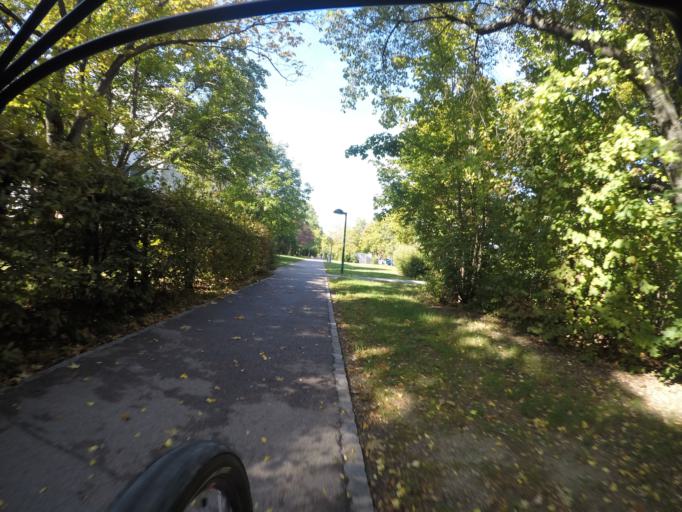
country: AT
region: Lower Austria
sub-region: Politischer Bezirk Modling
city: Wiener Neudorf
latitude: 48.0941
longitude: 16.3060
